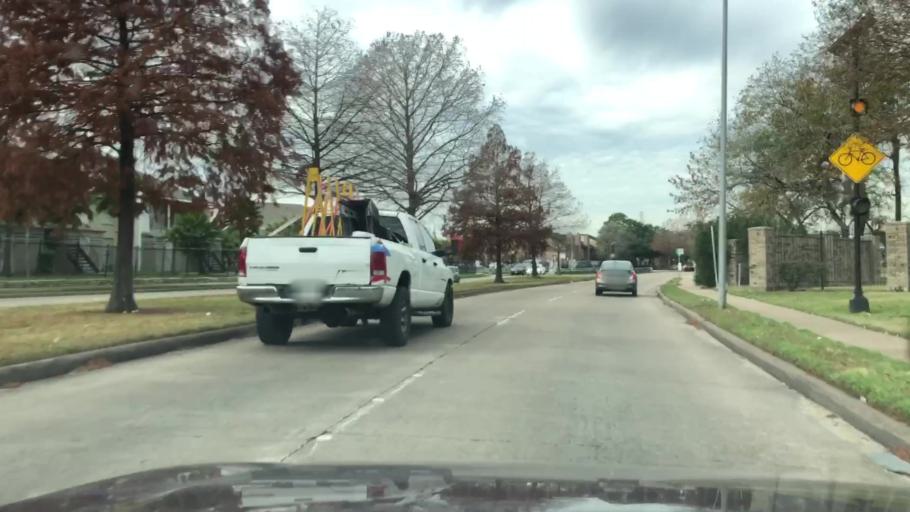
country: US
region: Texas
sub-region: Fort Bend County
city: Missouri City
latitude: 29.6720
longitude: -95.5321
